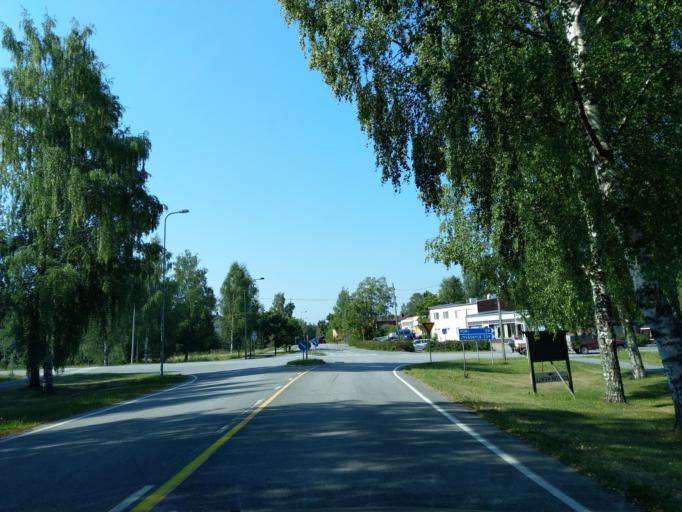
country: FI
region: Satakunta
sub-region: Pori
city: Pomarkku
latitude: 61.6986
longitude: 22.0144
